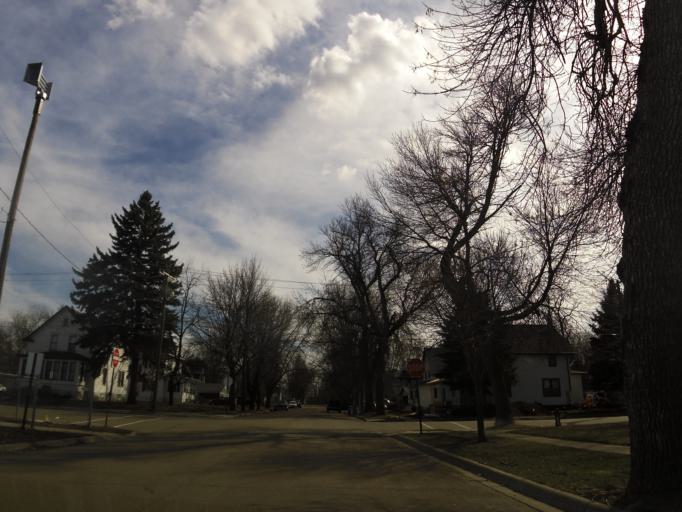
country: US
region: Minnesota
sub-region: Lac qui Parle County
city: Dawson
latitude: 44.9312
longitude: -96.0602
